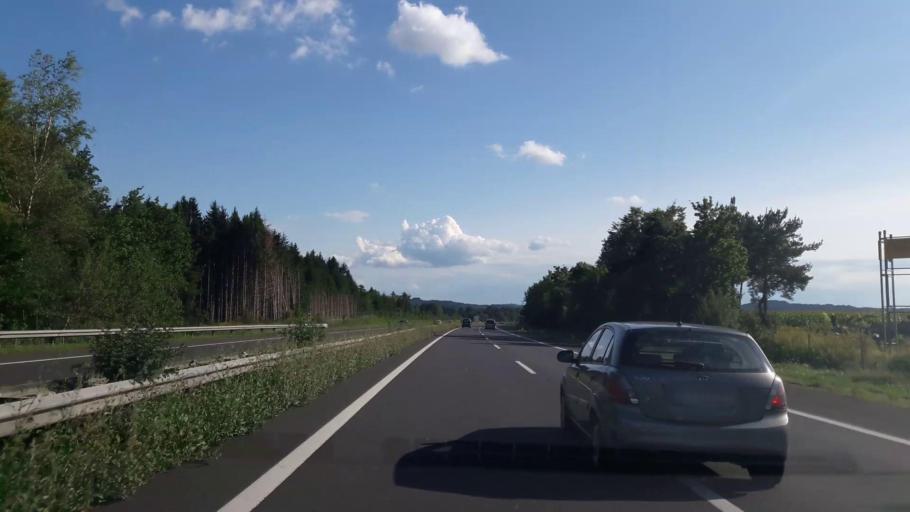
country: AT
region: Styria
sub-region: Politischer Bezirk Hartberg-Fuerstenfeld
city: Hainersdorf
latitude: 47.1059
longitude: 15.9849
